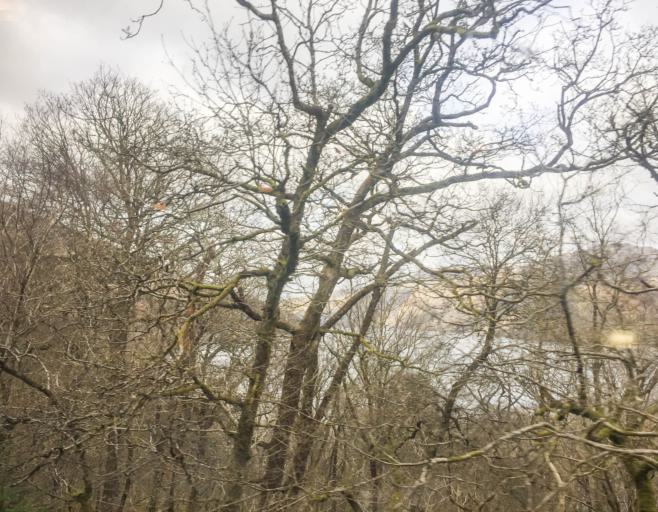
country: GB
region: Scotland
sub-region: Argyll and Bute
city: Garelochhead
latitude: 56.2381
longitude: -4.7078
